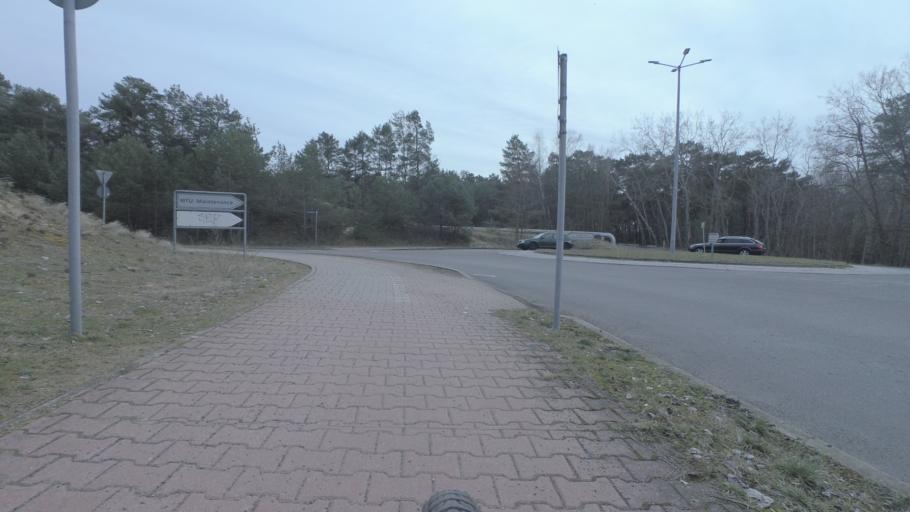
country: DE
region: Brandenburg
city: Ludwigsfelde
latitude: 52.3197
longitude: 13.2627
